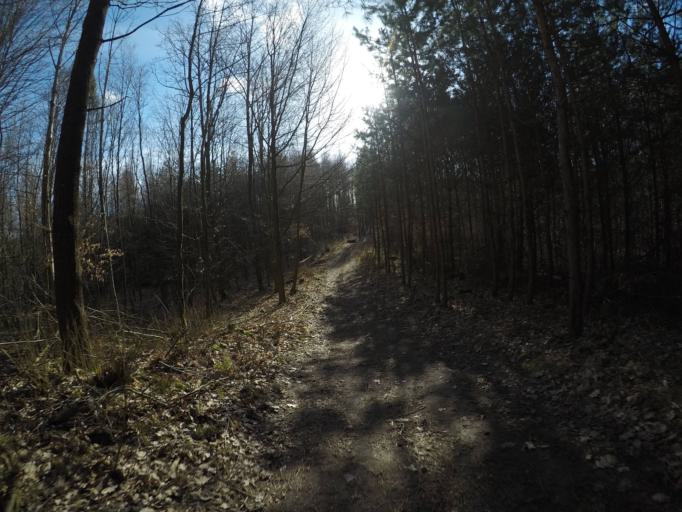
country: PL
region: Kujawsko-Pomorskie
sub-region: Powiat brodnicki
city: Gorzno
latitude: 53.1912
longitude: 19.6579
